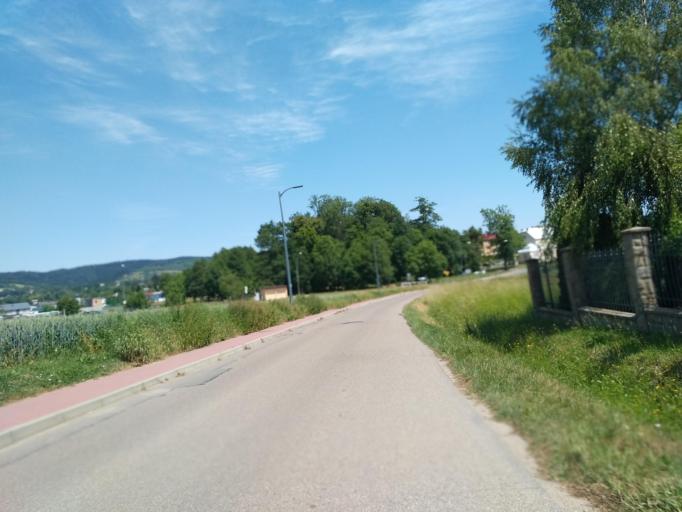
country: PL
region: Subcarpathian Voivodeship
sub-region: Powiat krosnienski
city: Korczyna
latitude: 49.7104
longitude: 21.8047
